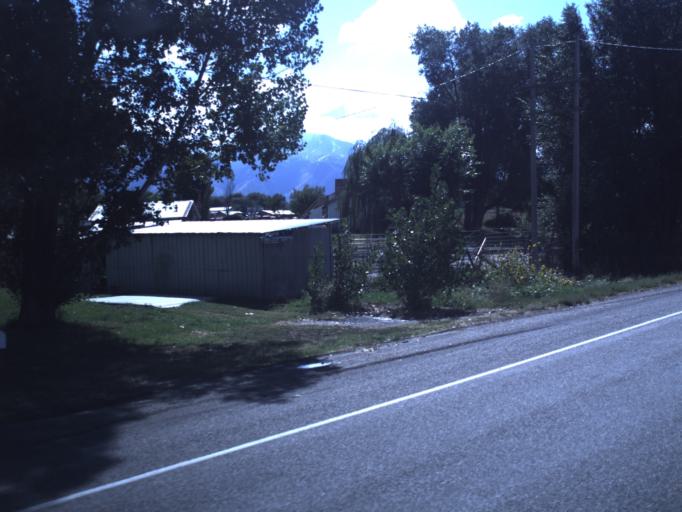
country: US
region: Utah
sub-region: Utah County
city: Springville
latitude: 40.1386
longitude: -111.6153
